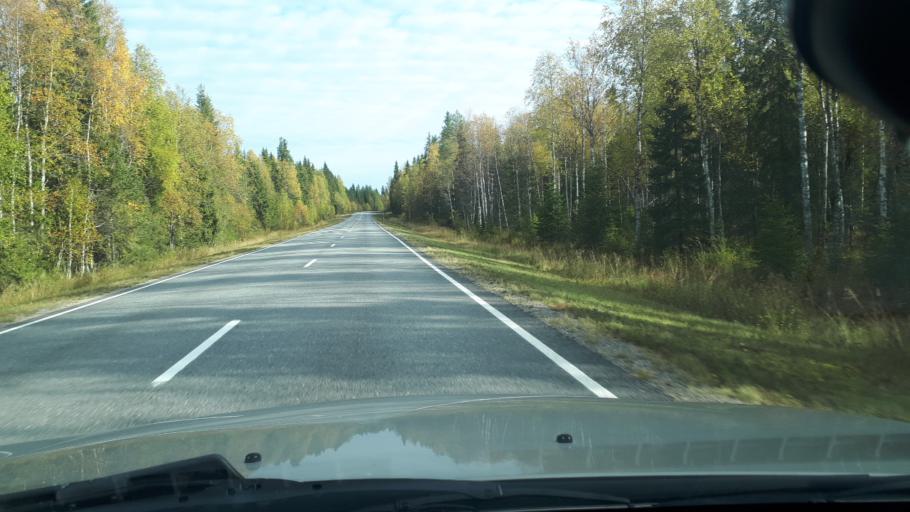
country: FI
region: Northern Ostrobothnia
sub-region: Oulu
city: Yli-Ii
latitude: 65.9481
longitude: 25.9048
